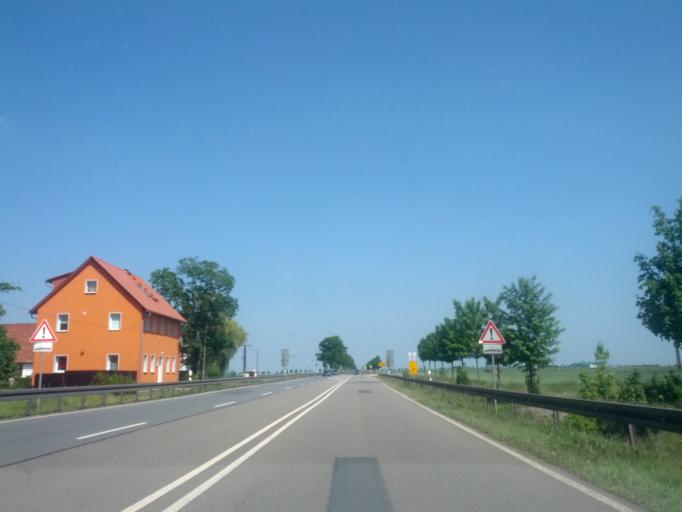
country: DE
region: Thuringia
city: Tuttleben
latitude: 50.9458
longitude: 10.8184
